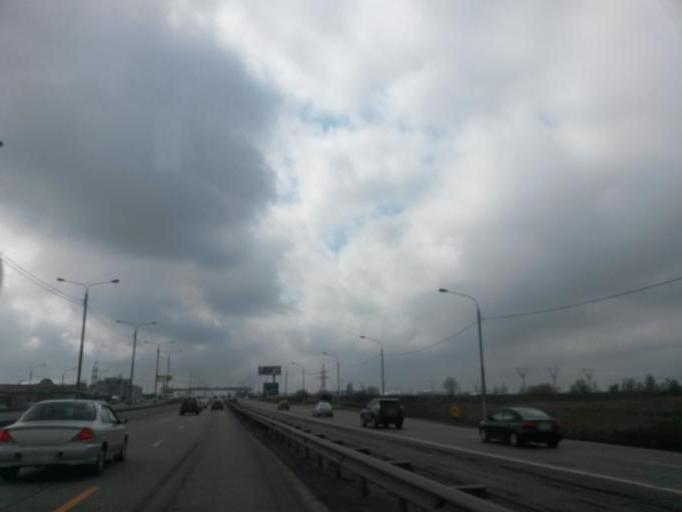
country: RU
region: Moskovskaya
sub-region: Podol'skiy Rayon
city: Podol'sk
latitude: 55.4528
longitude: 37.6181
